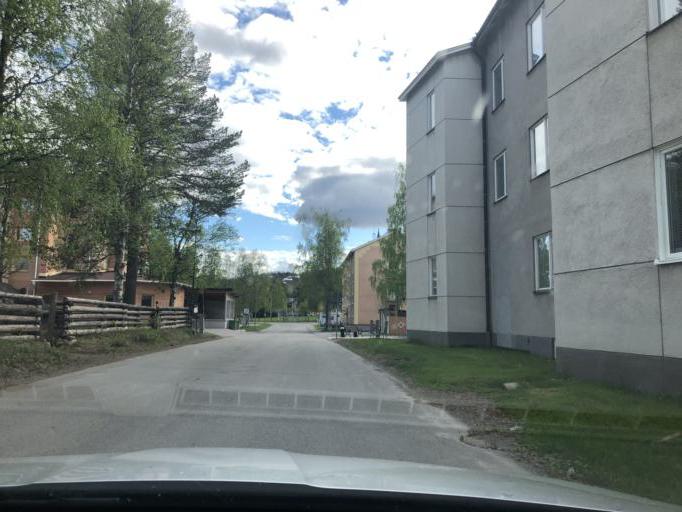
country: SE
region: Norrbotten
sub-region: Arvidsjaurs Kommun
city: Arvidsjaur
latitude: 65.5968
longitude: 19.1701
